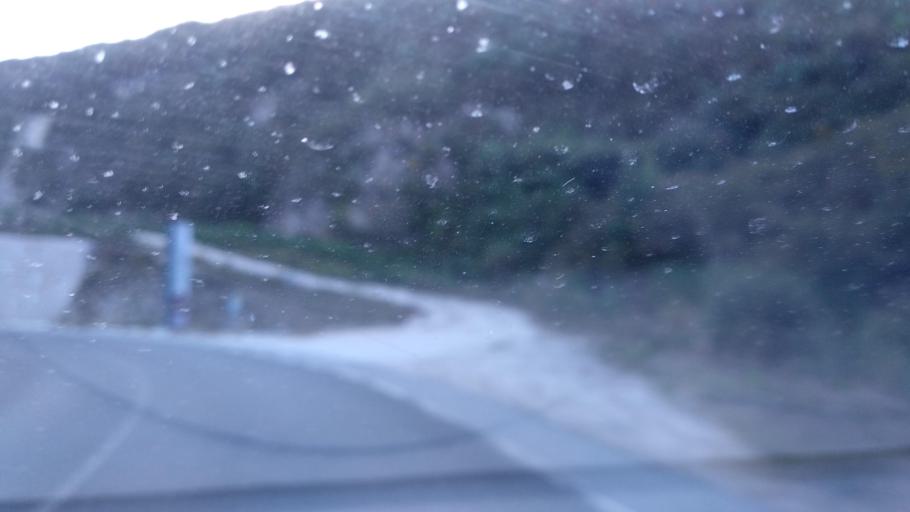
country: ES
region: Galicia
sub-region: Provincia de Pontevedra
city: Ponte Caldelas
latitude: 42.3409
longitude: -8.5478
